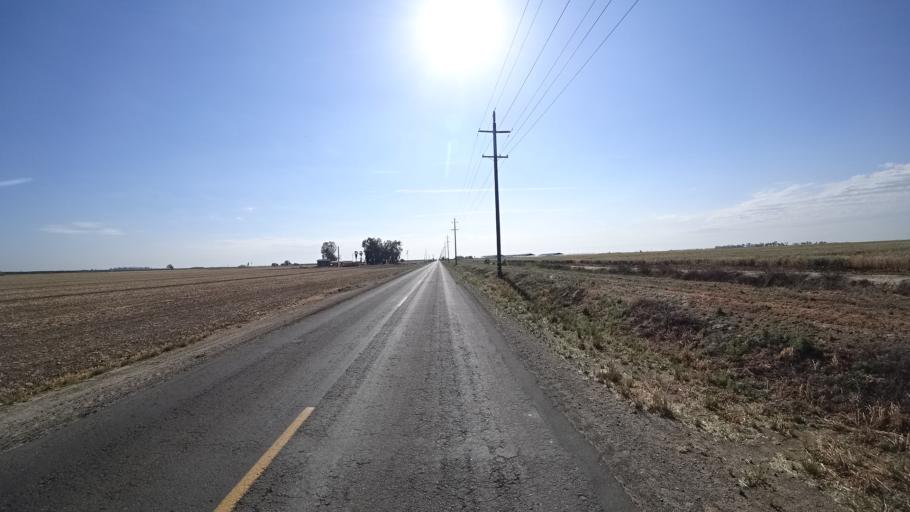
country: US
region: California
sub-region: Kings County
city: Armona
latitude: 36.2256
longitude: -119.7242
